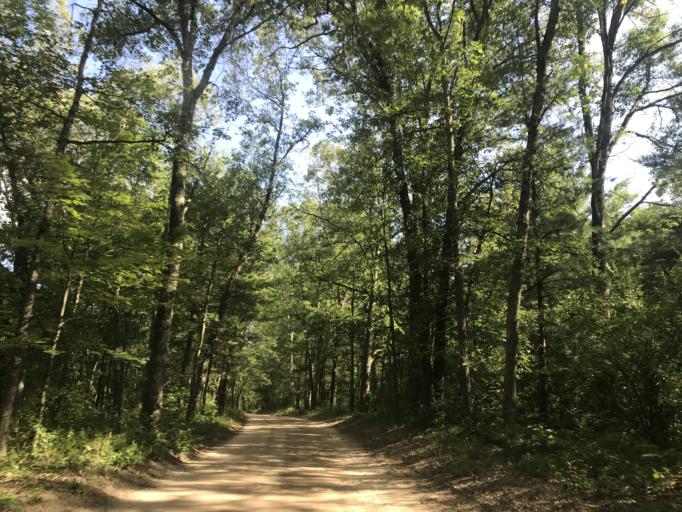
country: US
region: Michigan
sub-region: Newaygo County
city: Newaygo
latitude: 43.4641
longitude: -85.7646
